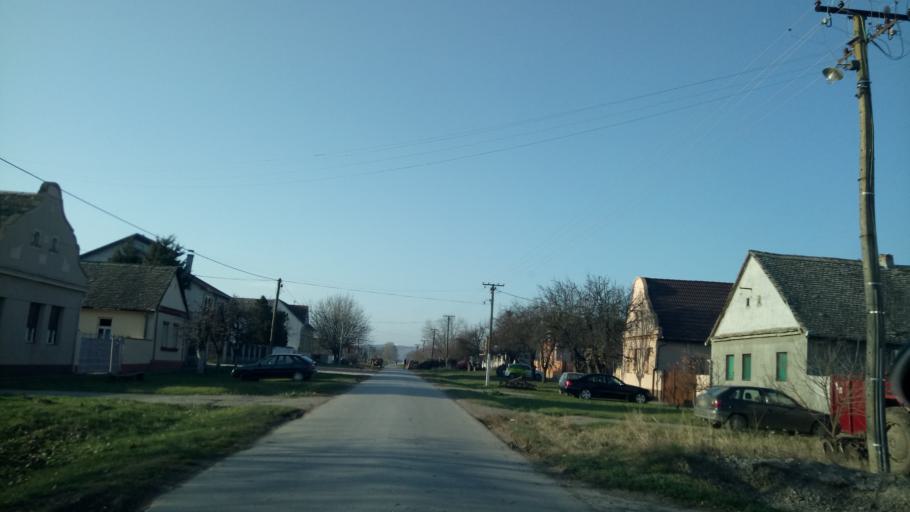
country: RS
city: Novi Slankamen
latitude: 45.1307
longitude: 20.2359
